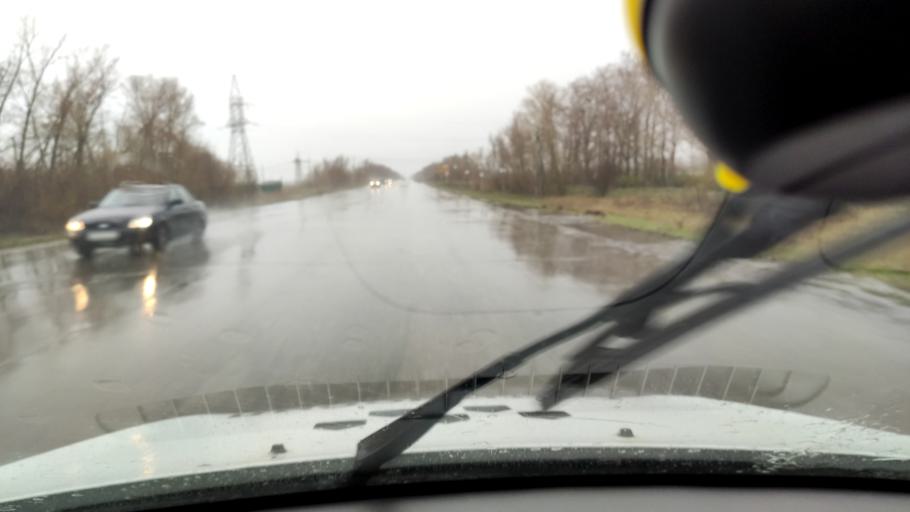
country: RU
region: Samara
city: Tol'yatti
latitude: 53.5842
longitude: 49.4045
